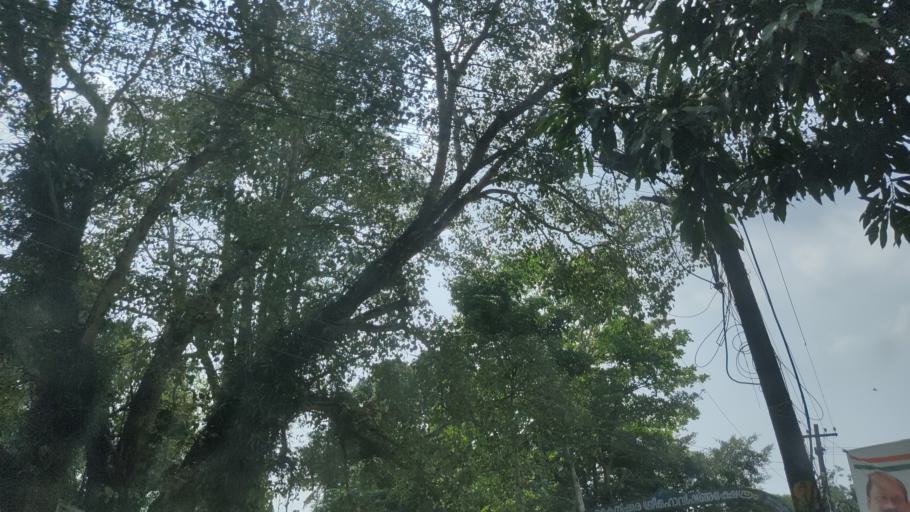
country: IN
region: Kerala
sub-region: Pattanamtitta
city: Tiruvalla
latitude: 9.3322
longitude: 76.5323
